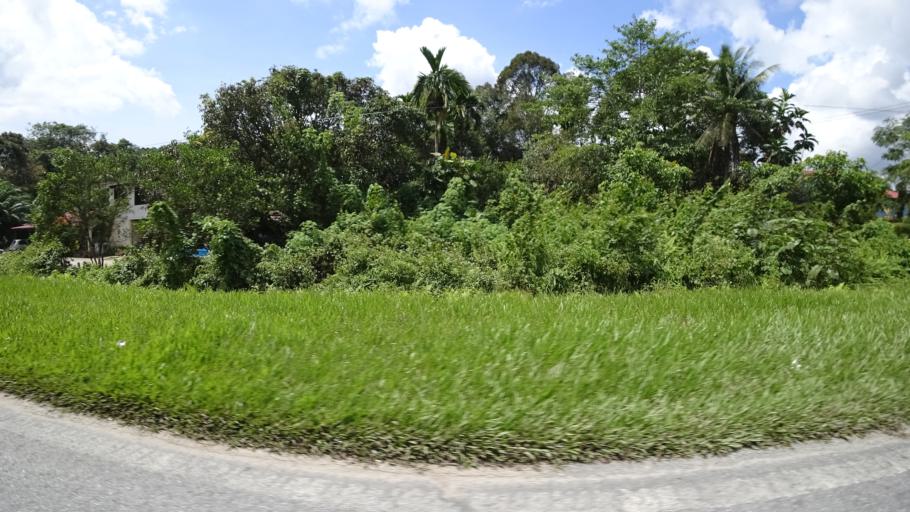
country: BN
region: Tutong
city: Tutong
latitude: 4.6834
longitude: 114.8100
